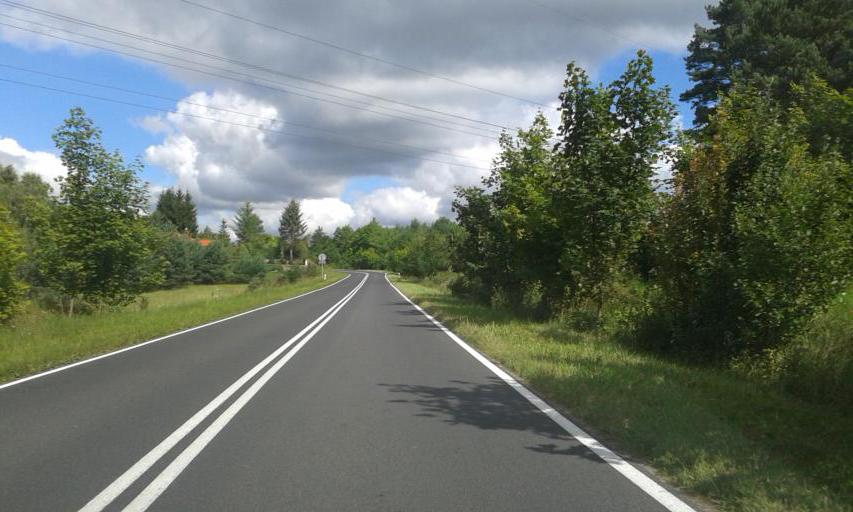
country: PL
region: West Pomeranian Voivodeship
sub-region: Powiat koszalinski
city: Polanow
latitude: 54.0329
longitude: 16.7191
